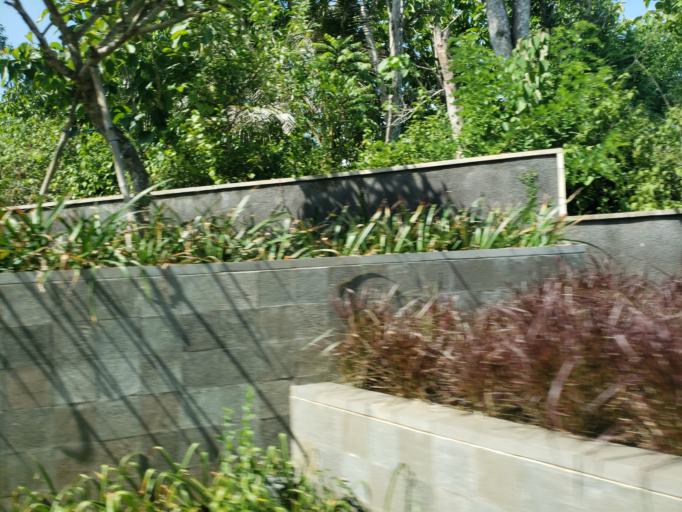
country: ID
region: Bali
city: Kangin
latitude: -8.8414
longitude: 115.1276
